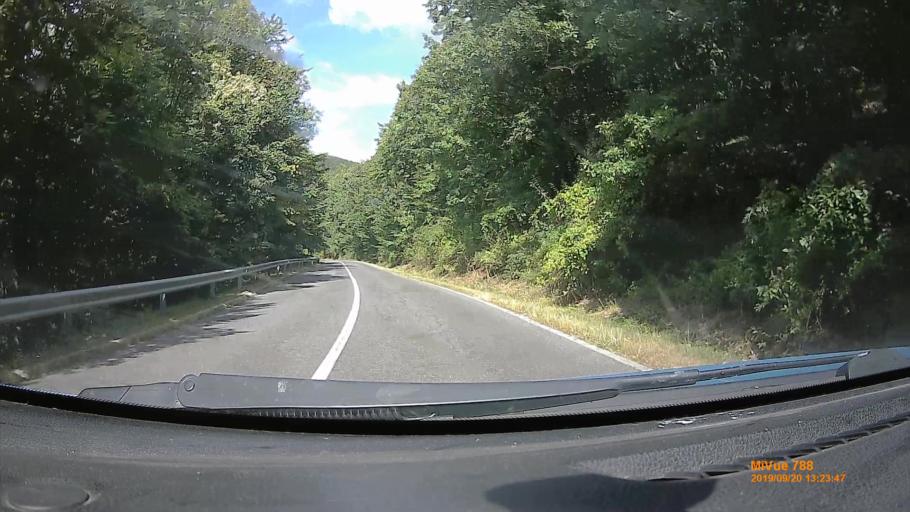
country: HU
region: Heves
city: Felsotarkany
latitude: 48.0344
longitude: 20.4791
